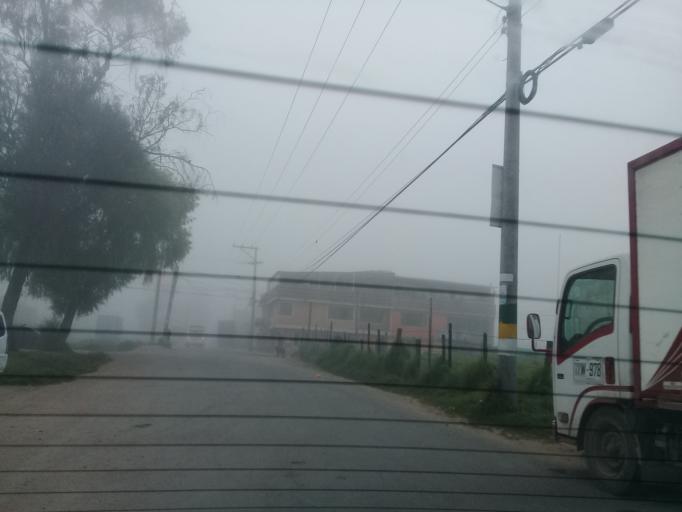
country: CO
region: Cundinamarca
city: Madrid
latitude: 4.7324
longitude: -74.2505
